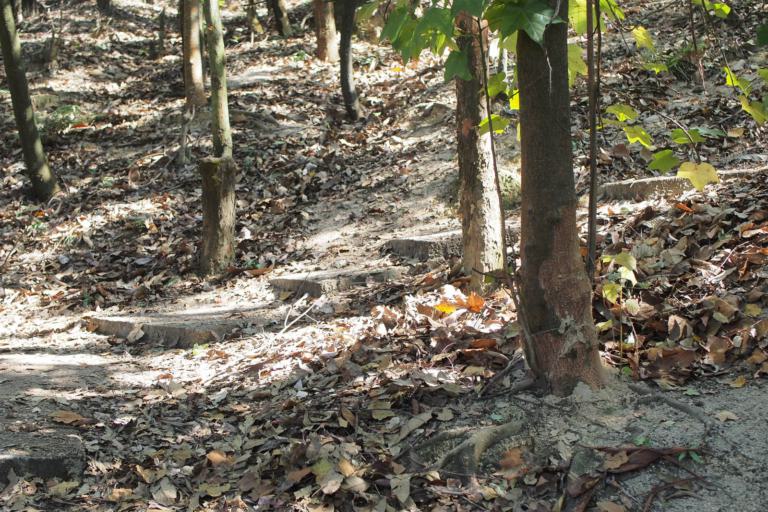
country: CN
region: Guangdong
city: Huancheng
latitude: 22.4636
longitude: 113.4164
